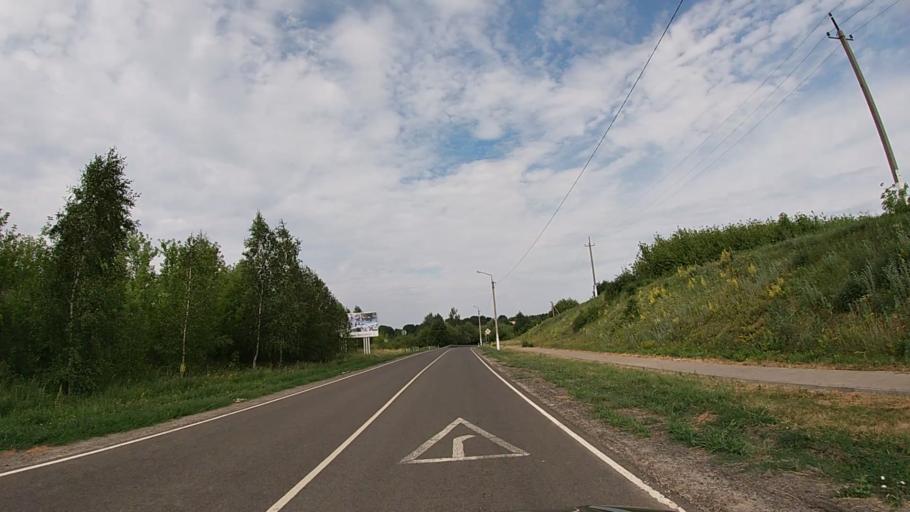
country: UA
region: Sumy
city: Krasnopillya
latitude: 50.8139
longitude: 35.4311
